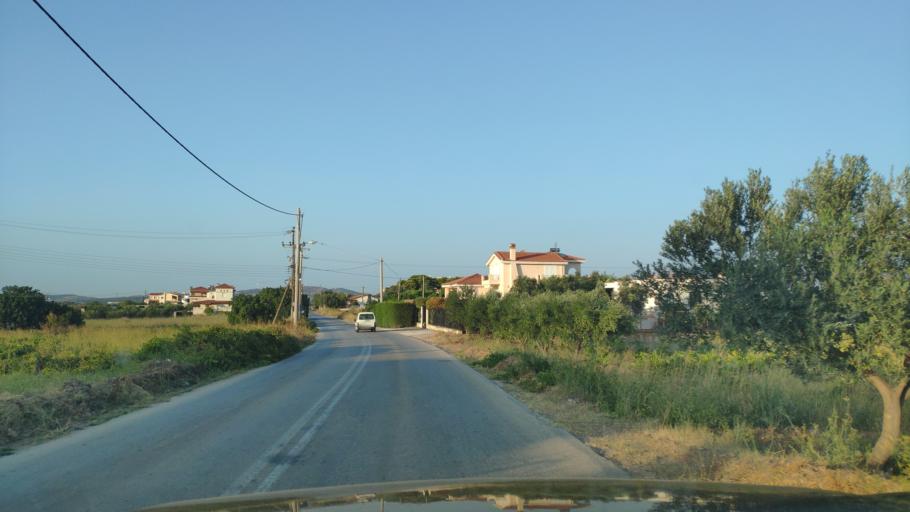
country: GR
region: Attica
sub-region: Nomarchia Anatolikis Attikis
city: Markopoulo
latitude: 37.9028
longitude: 23.9595
